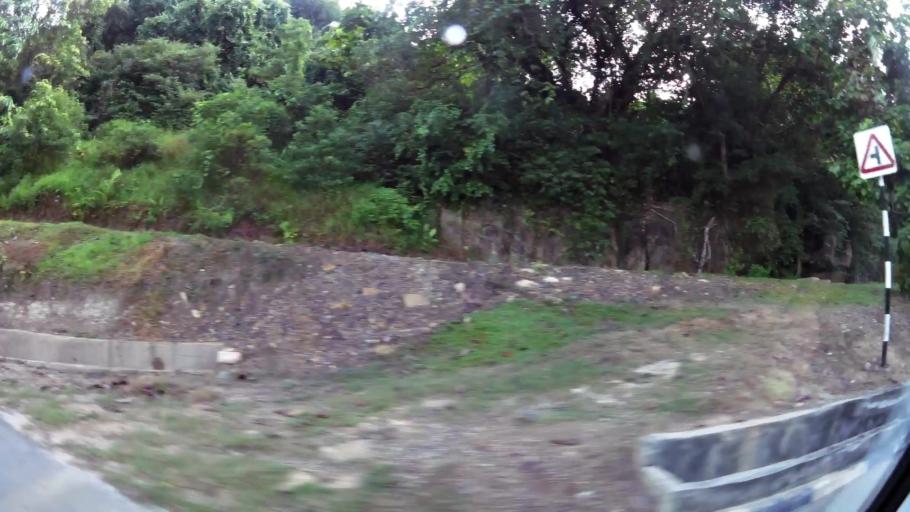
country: BN
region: Brunei and Muara
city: Bandar Seri Begawan
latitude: 4.8853
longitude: 114.9503
